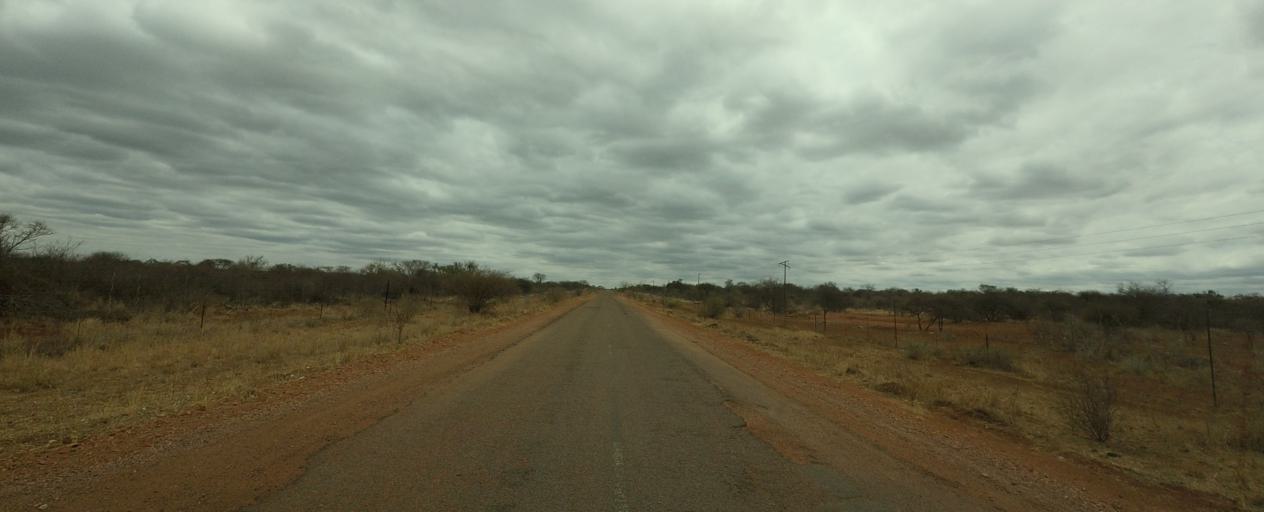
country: BW
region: Central
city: Mathathane
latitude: -22.7393
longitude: 28.4687
